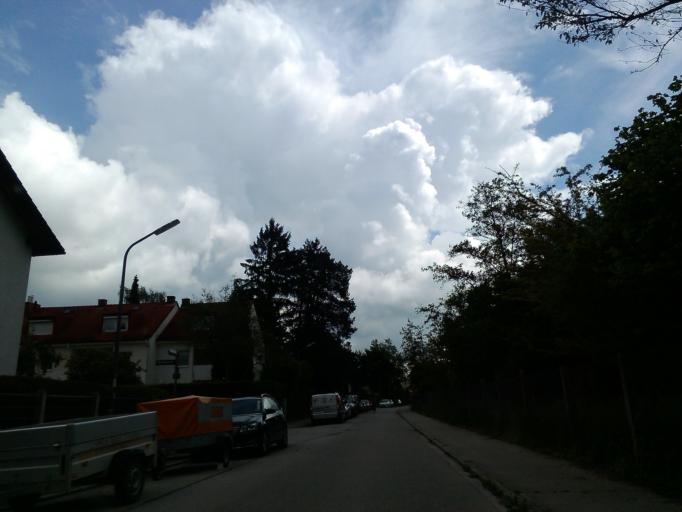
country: DE
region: Bavaria
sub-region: Upper Bavaria
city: Haar
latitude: 48.1106
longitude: 11.6884
